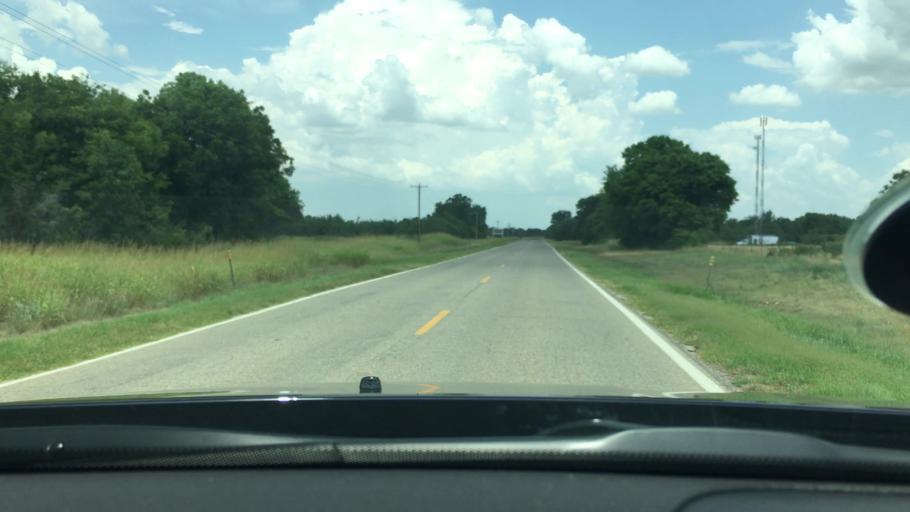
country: US
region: Oklahoma
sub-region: Marshall County
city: Oakland
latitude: 34.0097
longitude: -96.8793
